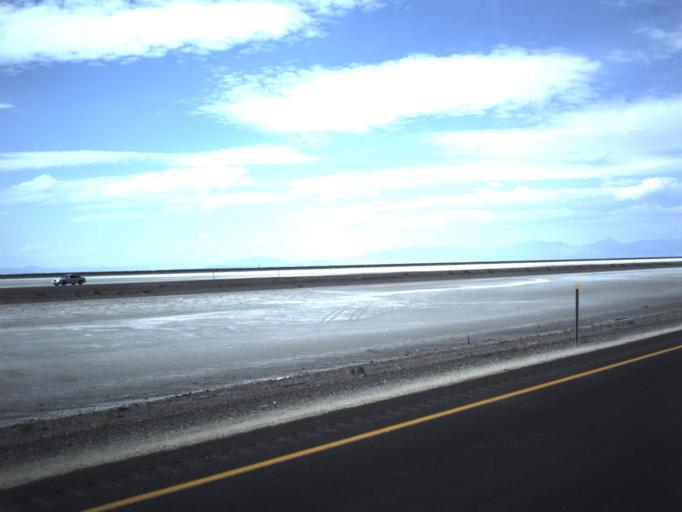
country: US
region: Utah
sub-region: Tooele County
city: Wendover
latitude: 40.7341
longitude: -113.5984
